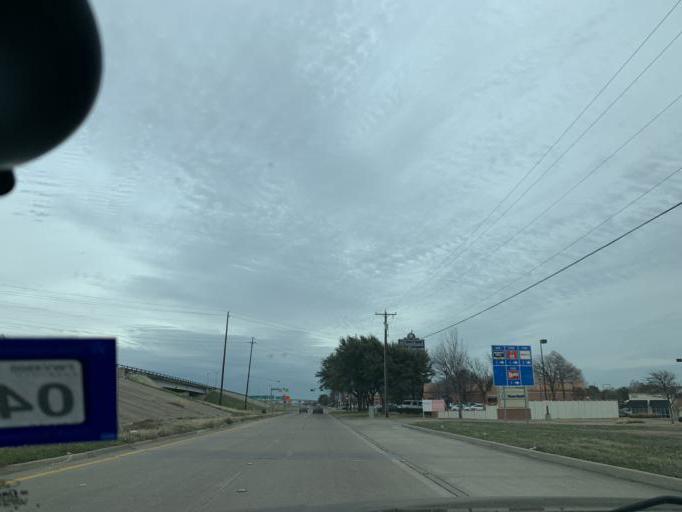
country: US
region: Texas
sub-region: Dallas County
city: Duncanville
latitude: 32.6466
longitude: -96.8850
